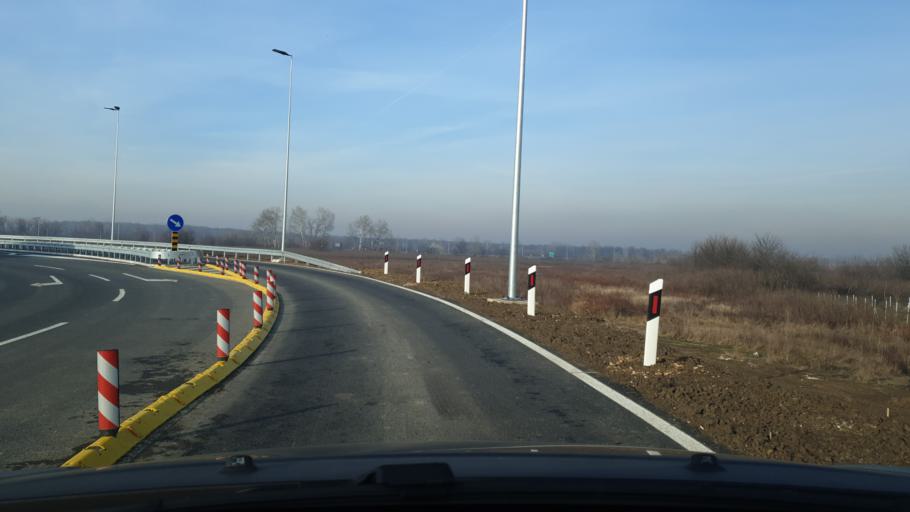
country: RS
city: Baric
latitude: 44.6511
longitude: 20.2377
